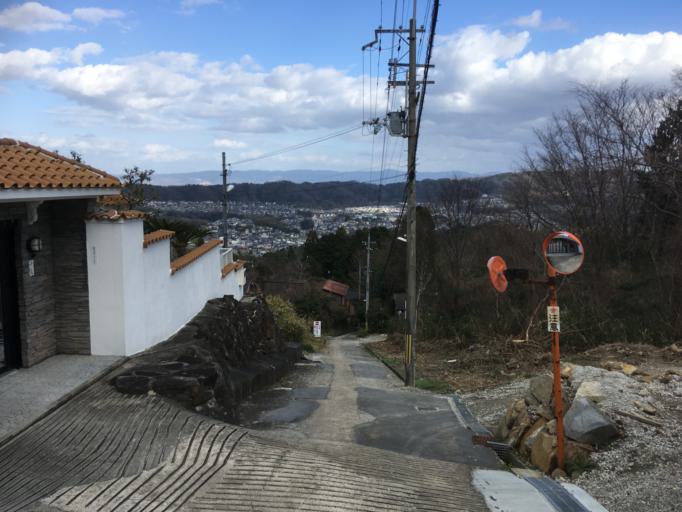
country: JP
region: Nara
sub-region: Ikoma-shi
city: Ikoma
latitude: 34.6754
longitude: 135.6918
